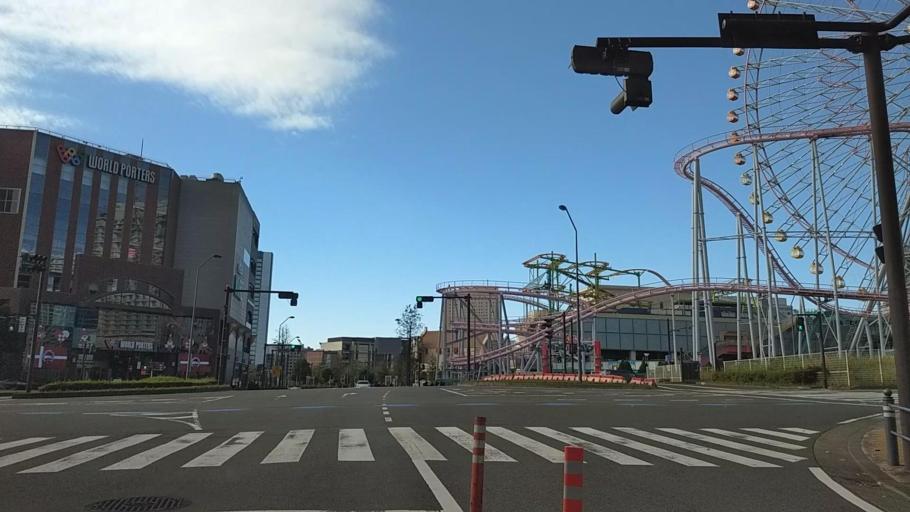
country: JP
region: Kanagawa
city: Yokohama
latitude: 35.4555
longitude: 139.6383
